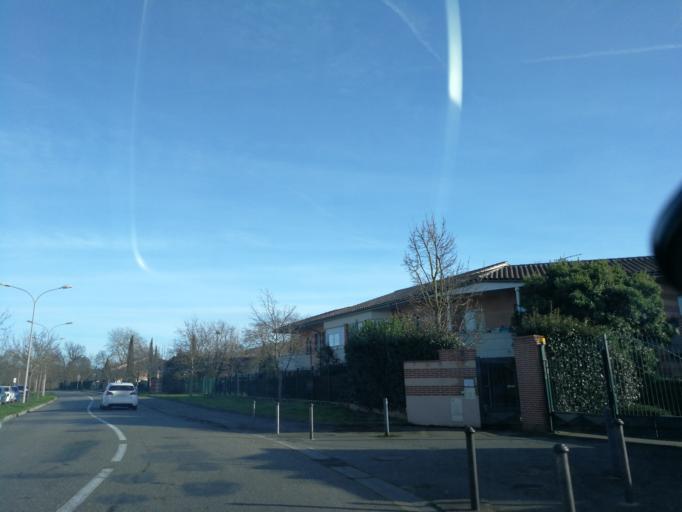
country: FR
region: Midi-Pyrenees
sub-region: Departement de la Haute-Garonne
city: L'Union
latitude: 43.6482
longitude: 1.4861
